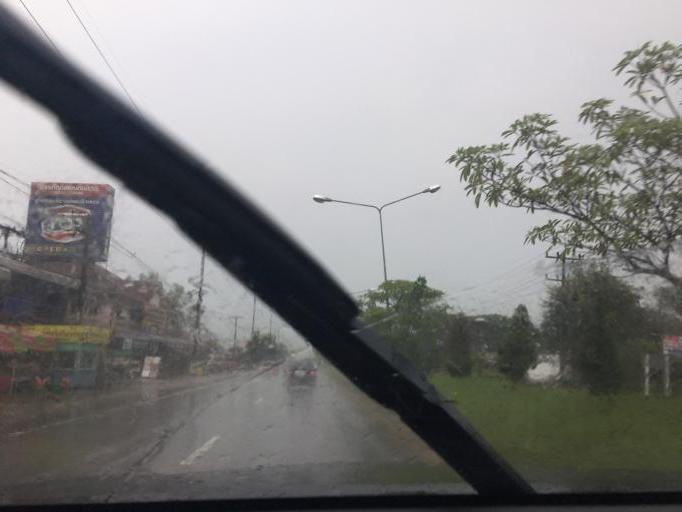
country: TH
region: Chiang Rai
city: Mae Fa Luang
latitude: 20.2421
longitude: 99.8561
